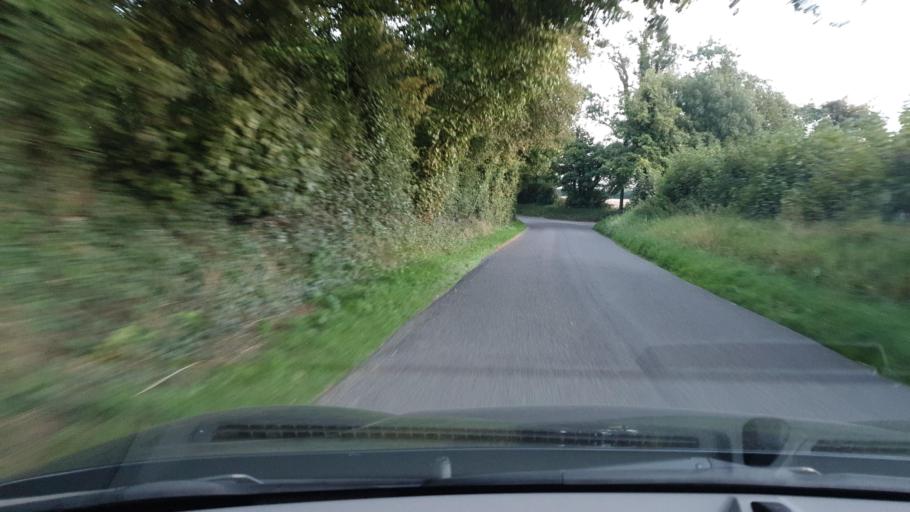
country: IE
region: Leinster
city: Balrothery
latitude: 53.5704
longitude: -6.1538
